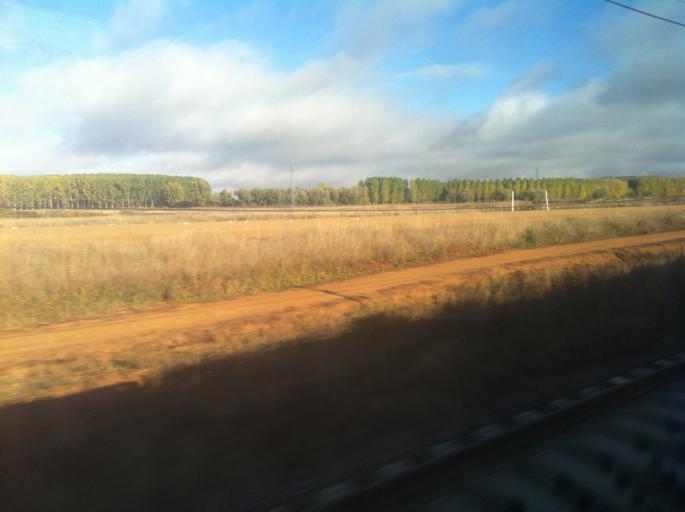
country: ES
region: Castille and Leon
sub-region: Provincia de Burgos
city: Buniel
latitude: 42.3242
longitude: -3.8156
